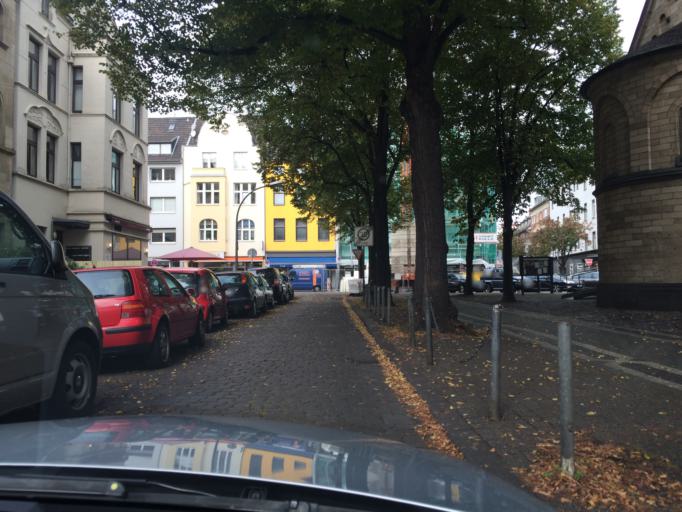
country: DE
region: North Rhine-Westphalia
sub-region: Regierungsbezirk Koln
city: Neustadt/Sued
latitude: 50.9188
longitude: 6.9269
